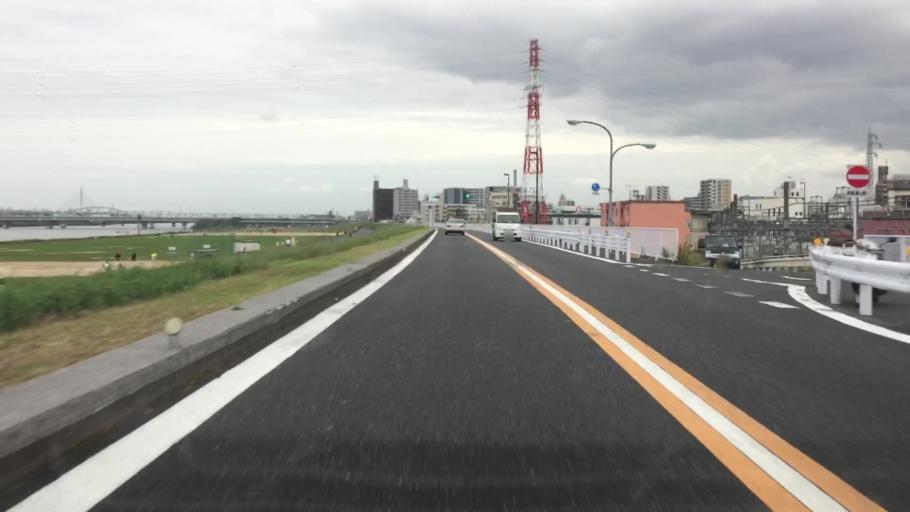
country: JP
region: Saitama
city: Soka
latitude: 35.7373
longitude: 139.8212
